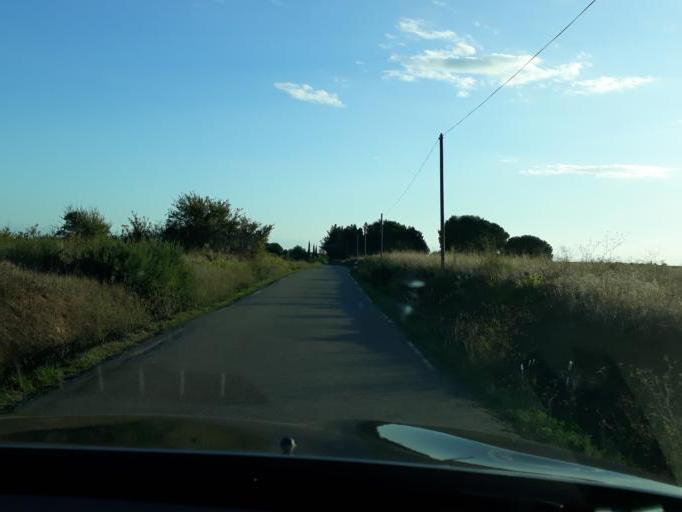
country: FR
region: Languedoc-Roussillon
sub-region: Departement de l'Herault
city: Pomerols
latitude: 43.3667
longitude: 3.4945
